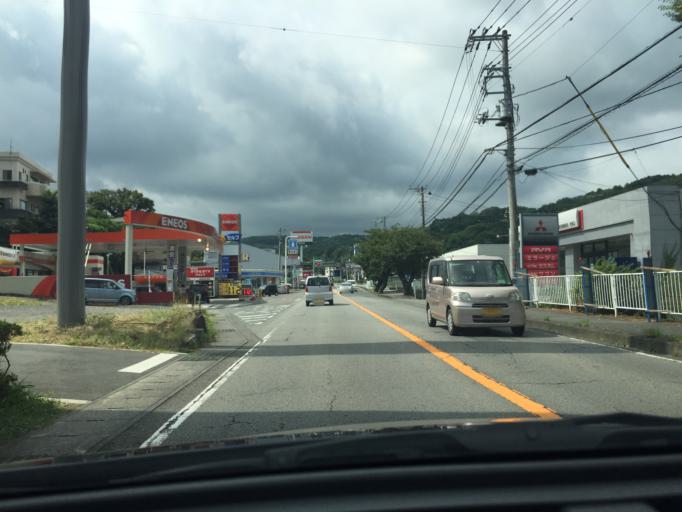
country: JP
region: Shizuoka
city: Ito
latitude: 34.9427
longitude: 139.1174
